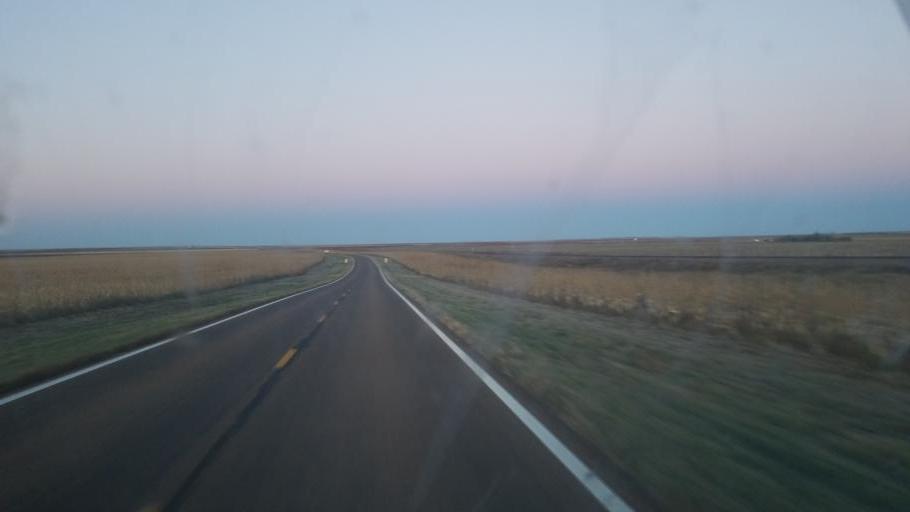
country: US
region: Kansas
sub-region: Wallace County
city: Sharon Springs
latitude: 38.9440
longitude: -101.5039
